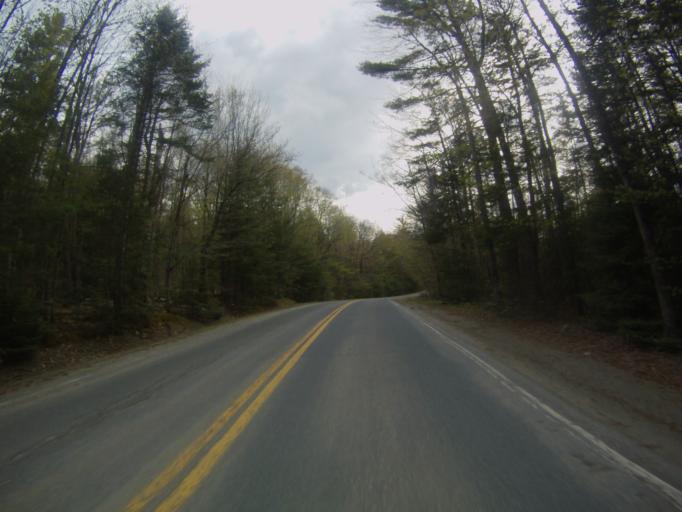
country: US
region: New York
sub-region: Warren County
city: Warrensburg
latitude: 43.8262
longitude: -73.9025
